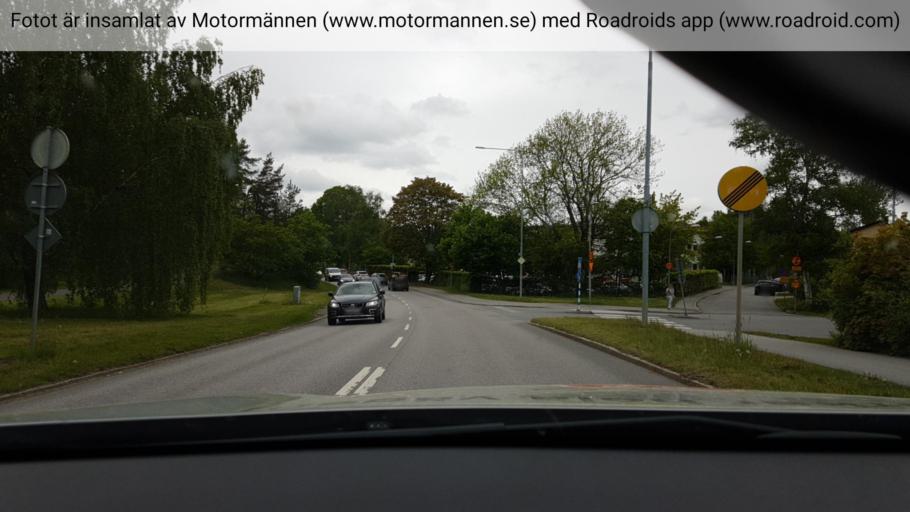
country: SE
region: Stockholm
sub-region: Lidingo
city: Lidingoe
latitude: 59.3618
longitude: 18.1555
